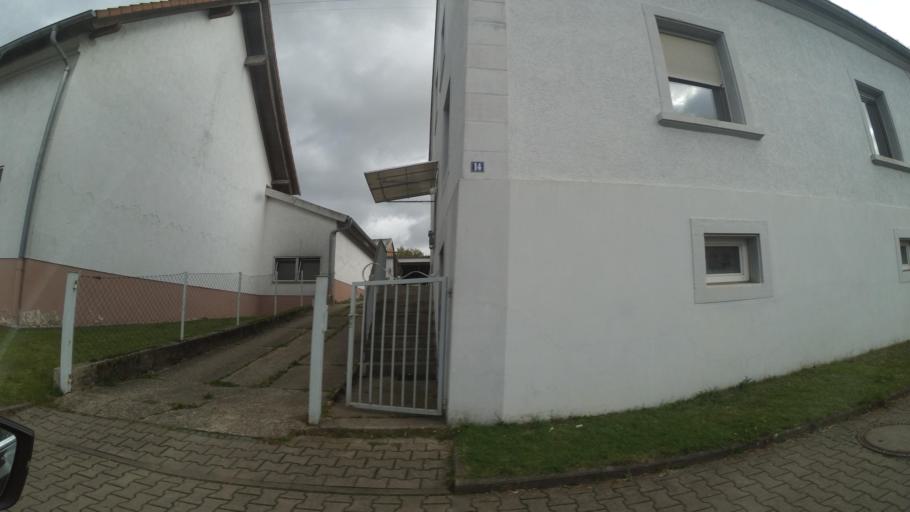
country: DE
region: Rheinland-Pfalz
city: Dietrichingen
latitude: 49.1880
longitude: 7.4140
